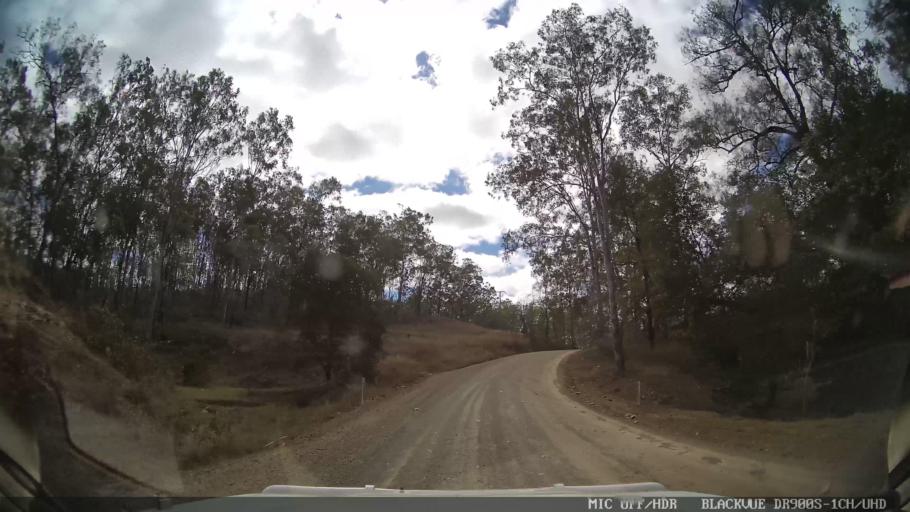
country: AU
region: Queensland
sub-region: Gladstone
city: Toolooa
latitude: -24.5530
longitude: 151.3363
